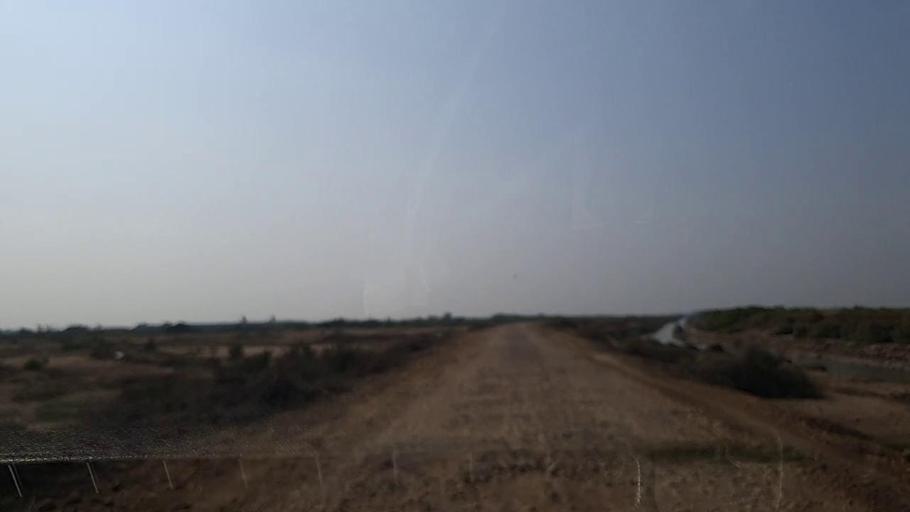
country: PK
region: Sindh
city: Mirpur Sakro
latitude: 24.6345
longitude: 67.7175
